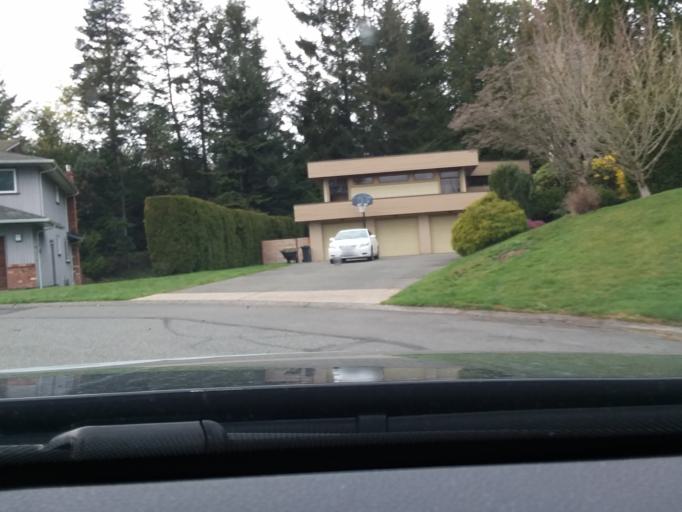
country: CA
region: British Columbia
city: North Saanich
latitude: 48.6152
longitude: -123.4287
